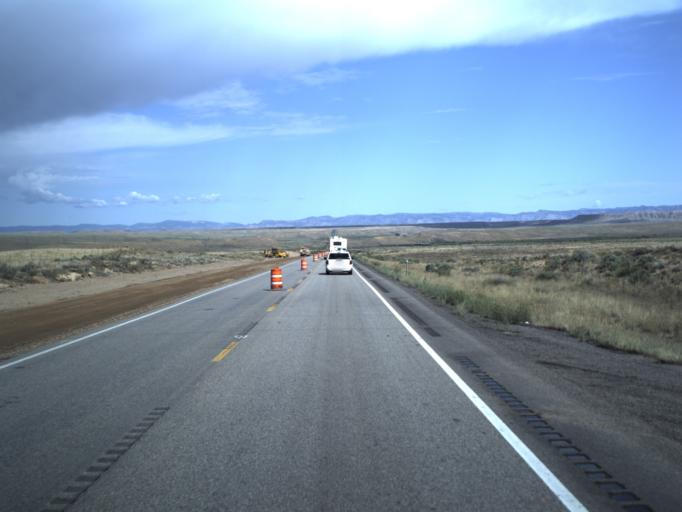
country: US
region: Utah
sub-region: Carbon County
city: East Carbon City
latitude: 39.4463
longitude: -110.4702
